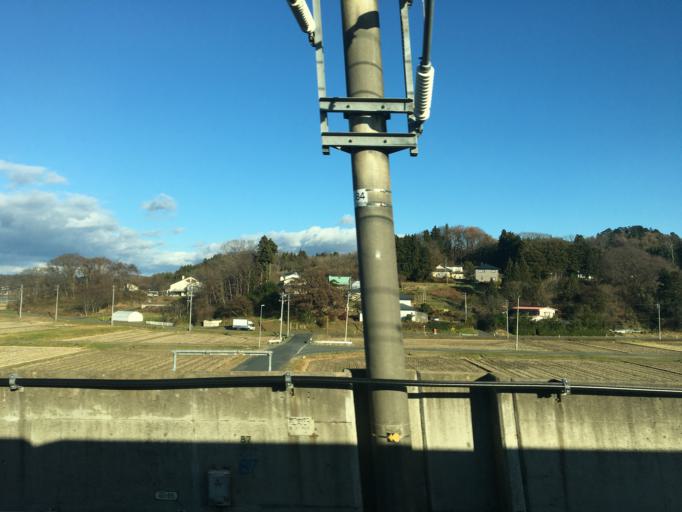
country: JP
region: Iwate
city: Mizusawa
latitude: 39.1499
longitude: 141.1872
